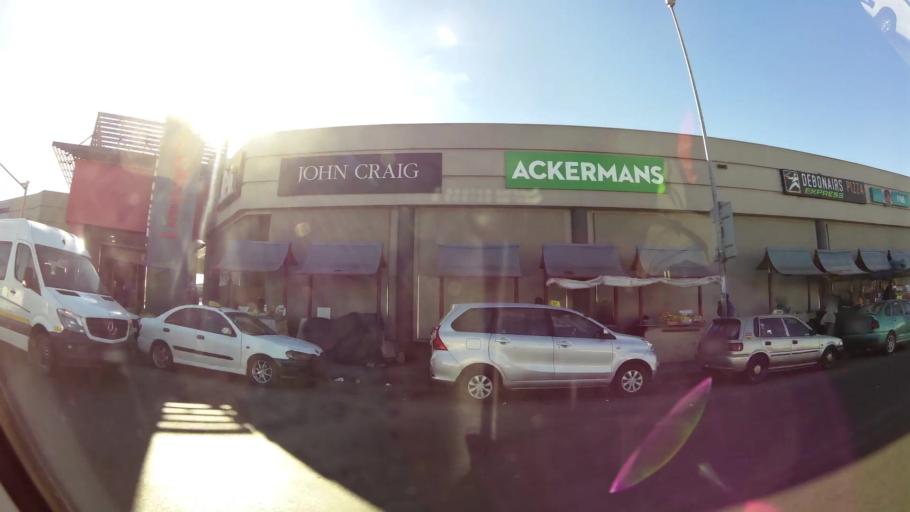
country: ZA
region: Limpopo
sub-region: Capricorn District Municipality
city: Polokwane
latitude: -23.9040
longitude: 29.4484
